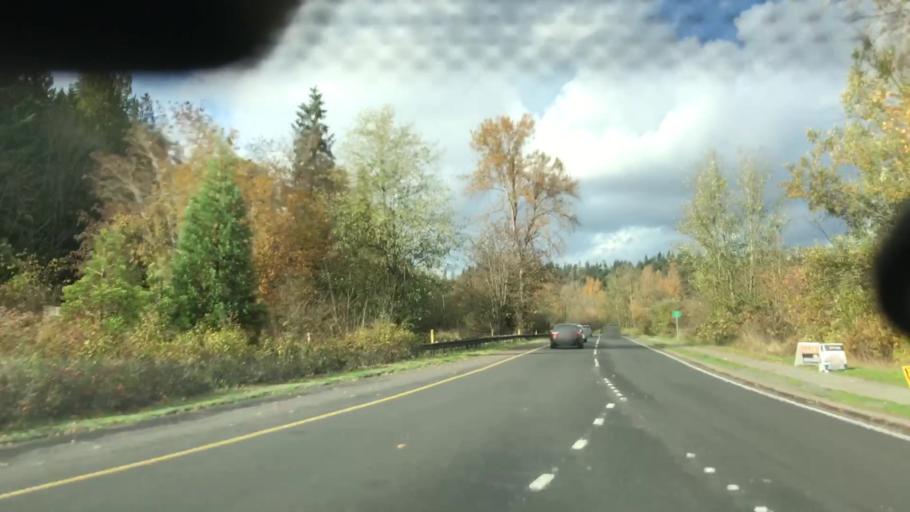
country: US
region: Washington
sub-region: King County
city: Newport
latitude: 47.5984
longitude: -122.1672
